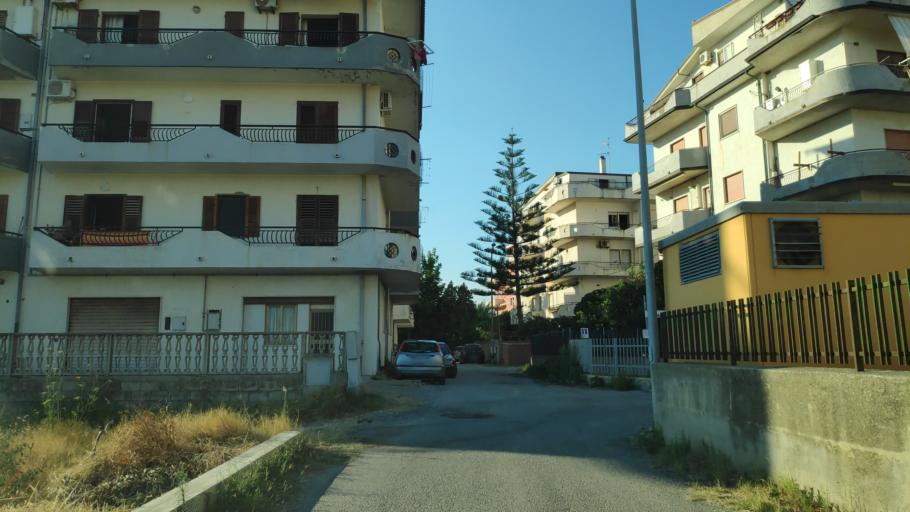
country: IT
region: Calabria
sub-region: Provincia di Reggio Calabria
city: Caulonia Marina
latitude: 38.3427
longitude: 16.4686
